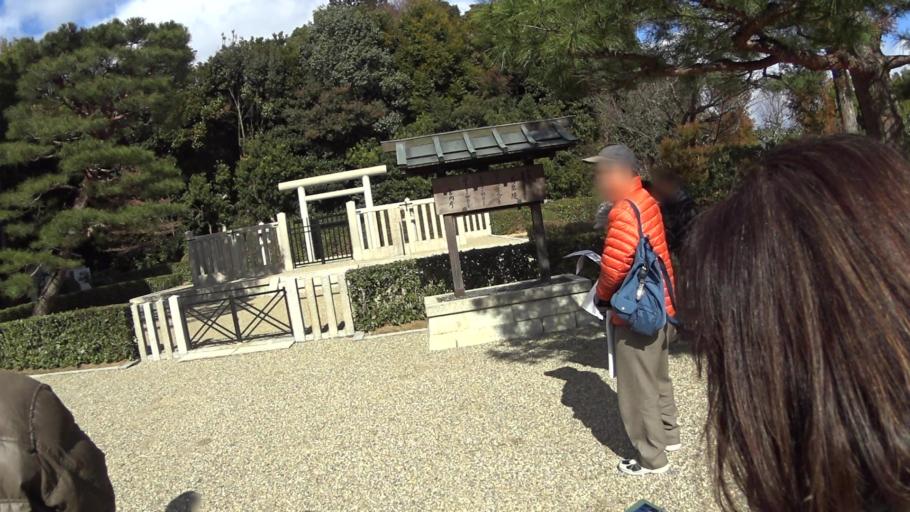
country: JP
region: Kyoto
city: Muko
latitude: 34.9535
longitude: 135.6932
